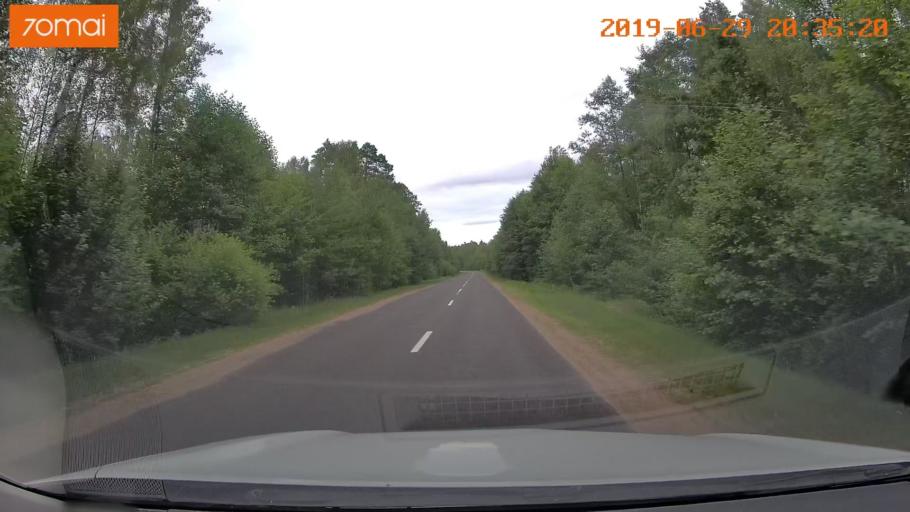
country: BY
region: Brest
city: Hantsavichy
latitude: 52.5159
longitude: 26.3482
